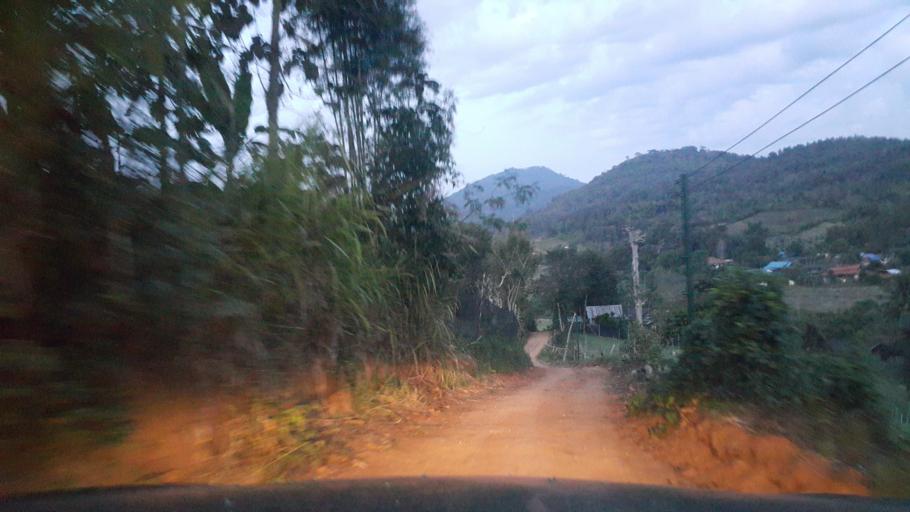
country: TH
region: Chiang Mai
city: Samoeng
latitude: 18.9549
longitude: 98.6742
